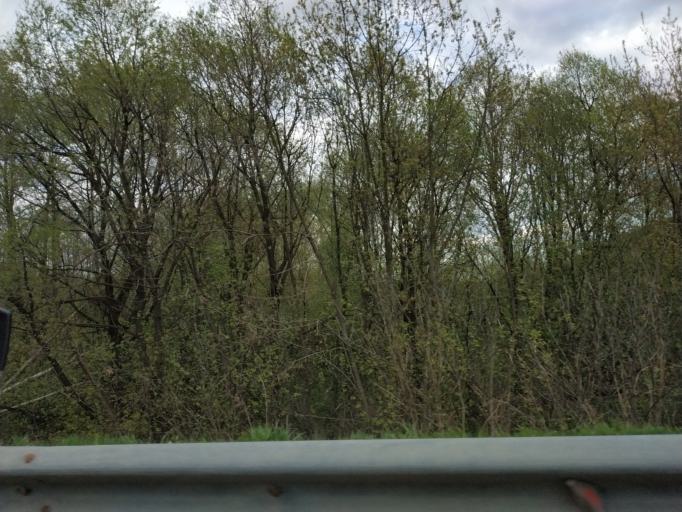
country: RU
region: Moskovskaya
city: Pavlovskiy Posad
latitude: 55.7991
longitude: 38.6524
